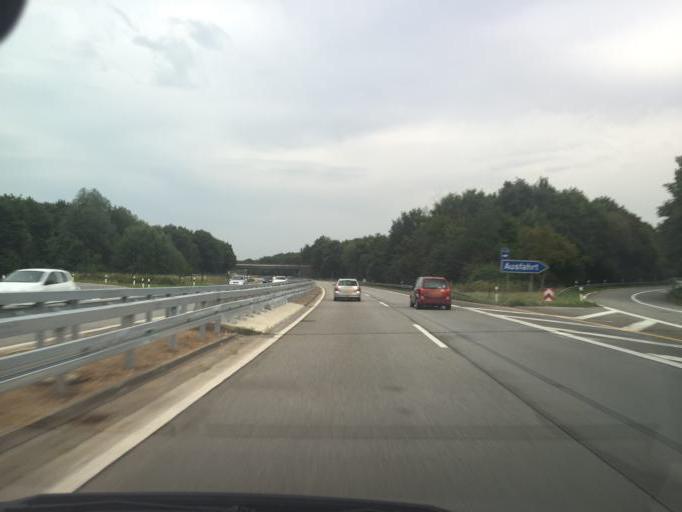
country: DE
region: North Rhine-Westphalia
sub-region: Regierungsbezirk Dusseldorf
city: Nettetal
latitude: 51.2855
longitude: 6.2713
